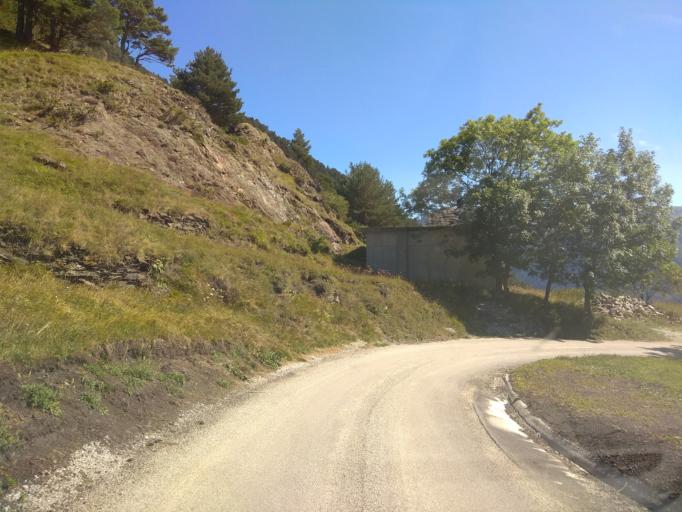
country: ES
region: Catalonia
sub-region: Provincia de Lleida
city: Les
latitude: 42.7591
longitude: 0.7117
